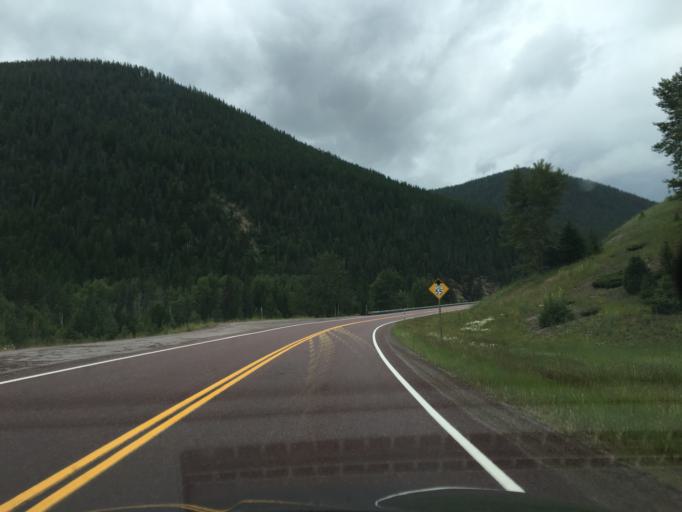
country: US
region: Montana
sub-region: Flathead County
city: Bigfork
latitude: 48.2342
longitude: -113.5651
